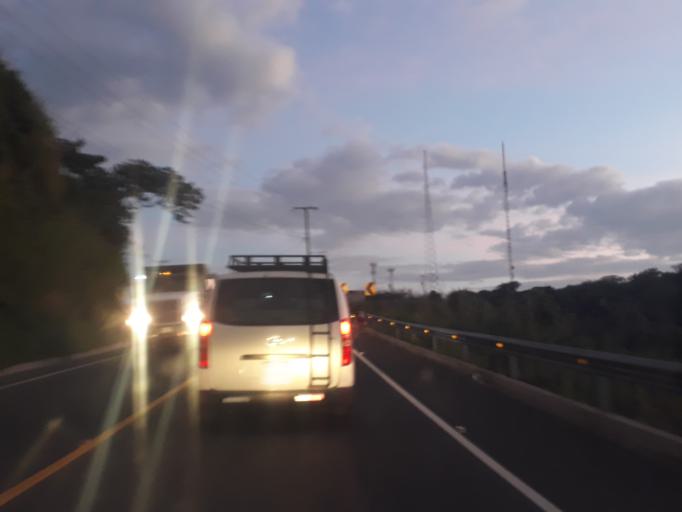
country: NI
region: Managua
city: El Crucero
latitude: 11.9940
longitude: -86.3095
